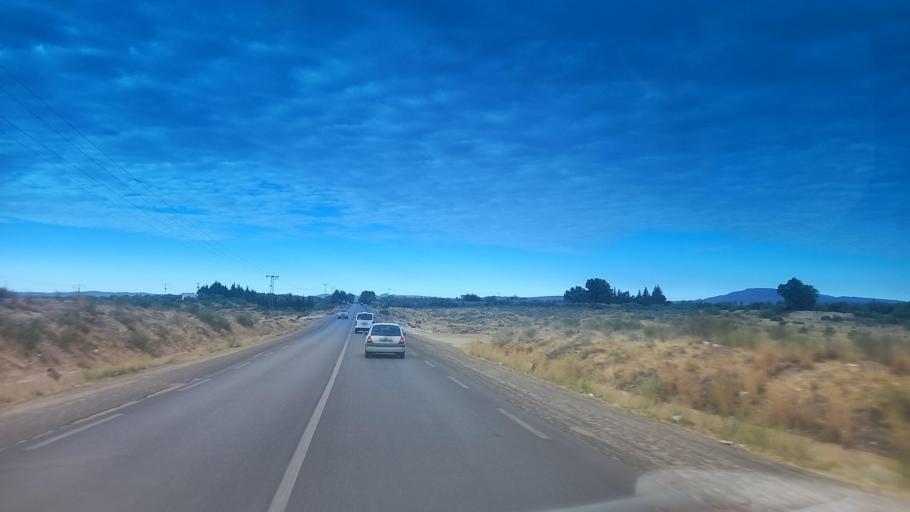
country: TN
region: Al Qasrayn
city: Sbiba
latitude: 35.2800
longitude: 9.0939
